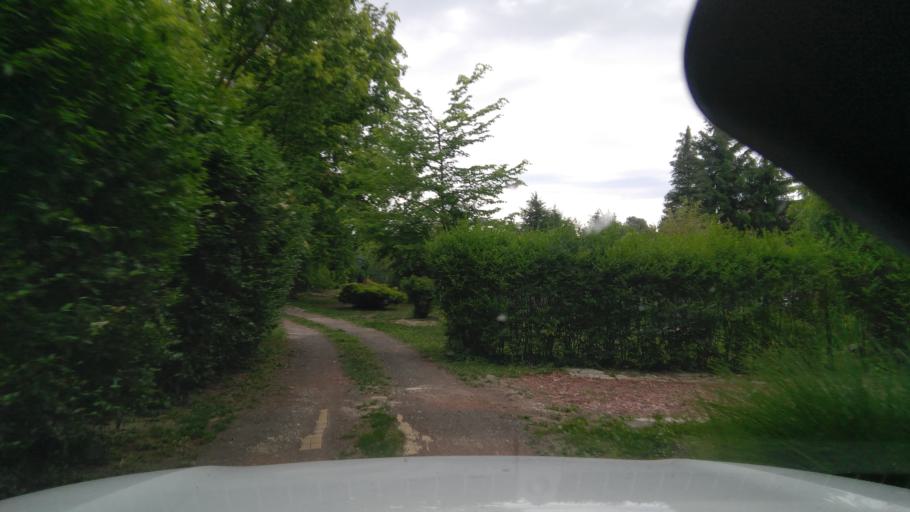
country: HU
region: Bekes
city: Doboz
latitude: 46.6719
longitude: 21.1894
